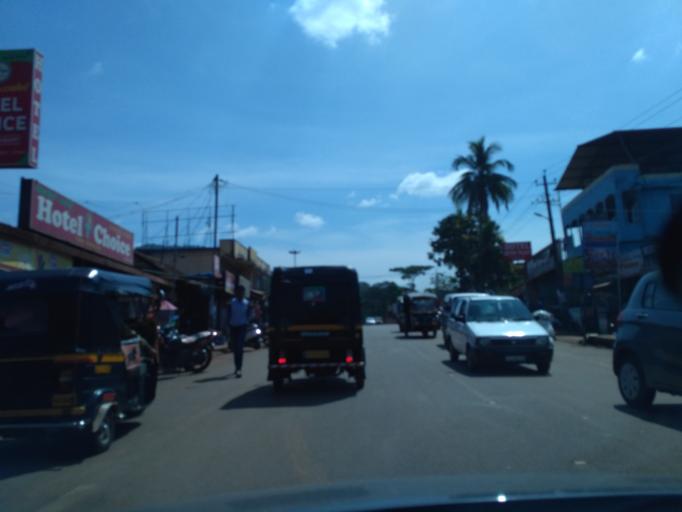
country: IN
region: Karnataka
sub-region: Dakshina Kannada
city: Sulya
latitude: 12.5545
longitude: 75.3951
